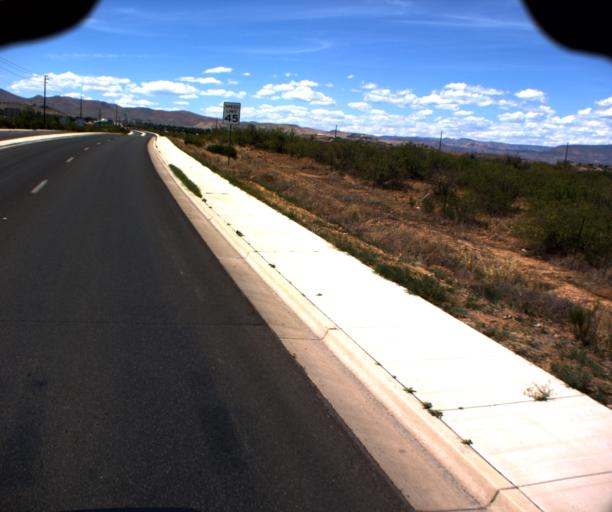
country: US
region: Arizona
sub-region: Yavapai County
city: Cottonwood
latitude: 34.7405
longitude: -112.0377
